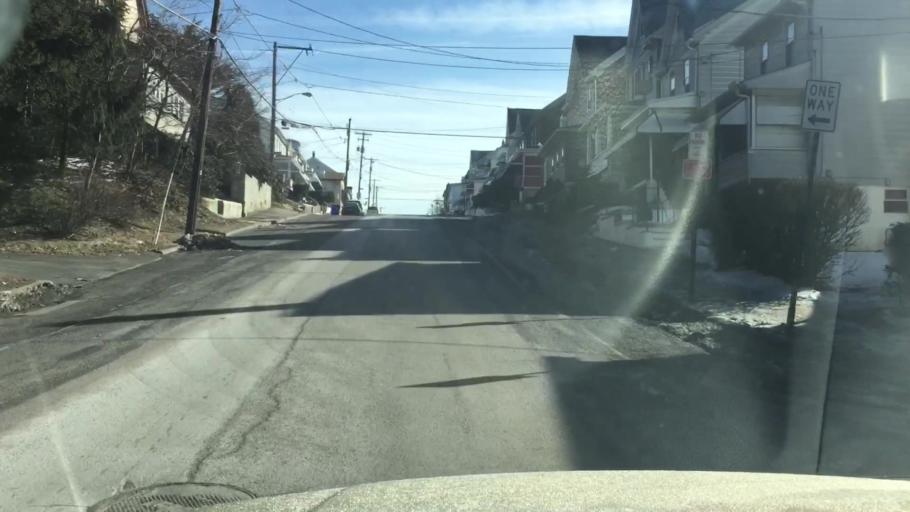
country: US
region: Pennsylvania
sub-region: Luzerne County
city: Hazleton
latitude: 40.9675
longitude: -75.9695
